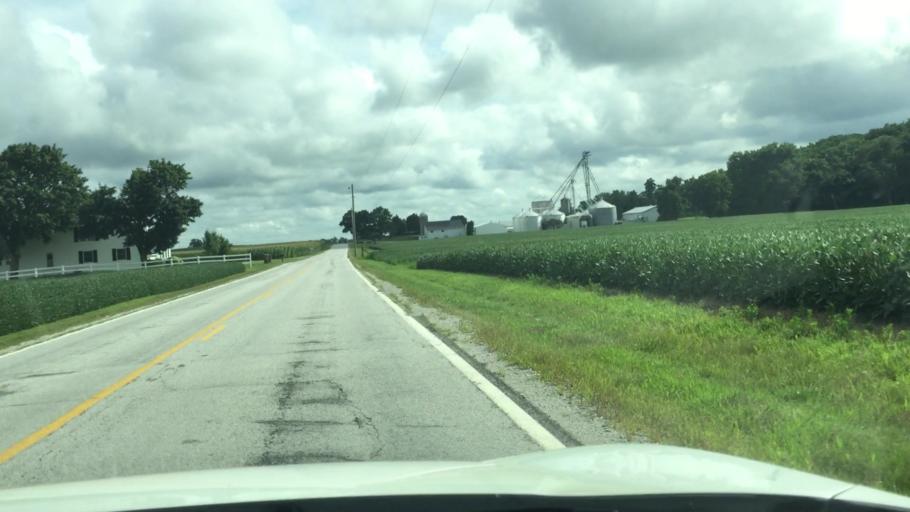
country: US
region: Ohio
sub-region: Clark County
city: Northridge
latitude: 39.9760
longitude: -83.6774
